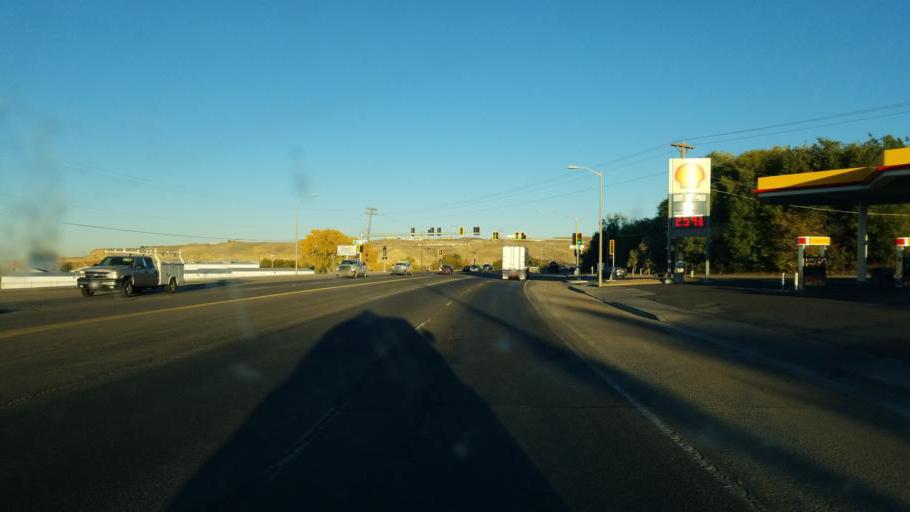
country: US
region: New Mexico
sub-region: San Juan County
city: Farmington
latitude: 36.7331
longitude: -108.2438
